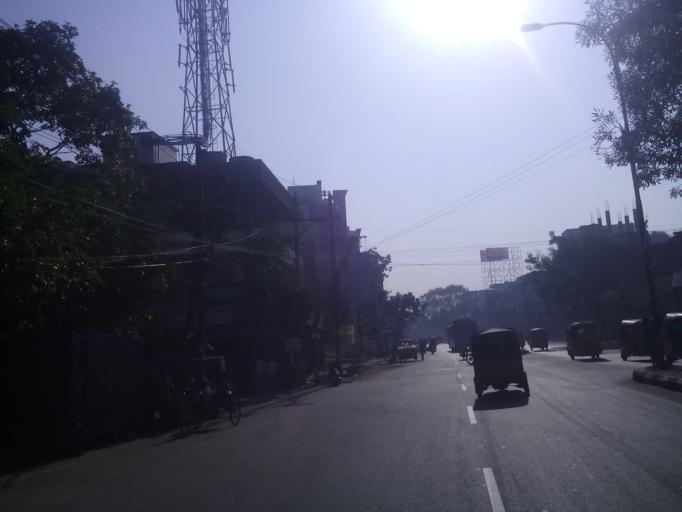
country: IN
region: Telangana
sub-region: Warangal
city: Warangal
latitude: 17.9906
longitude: 79.5947
